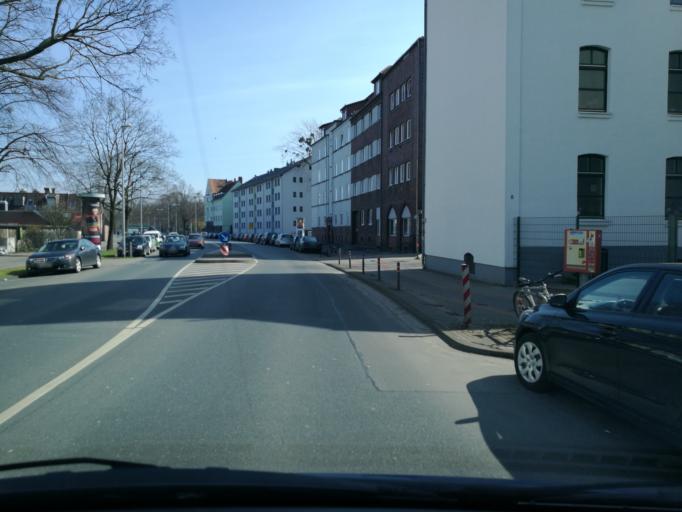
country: DE
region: Lower Saxony
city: Hannover
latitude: 52.3744
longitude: 9.6925
